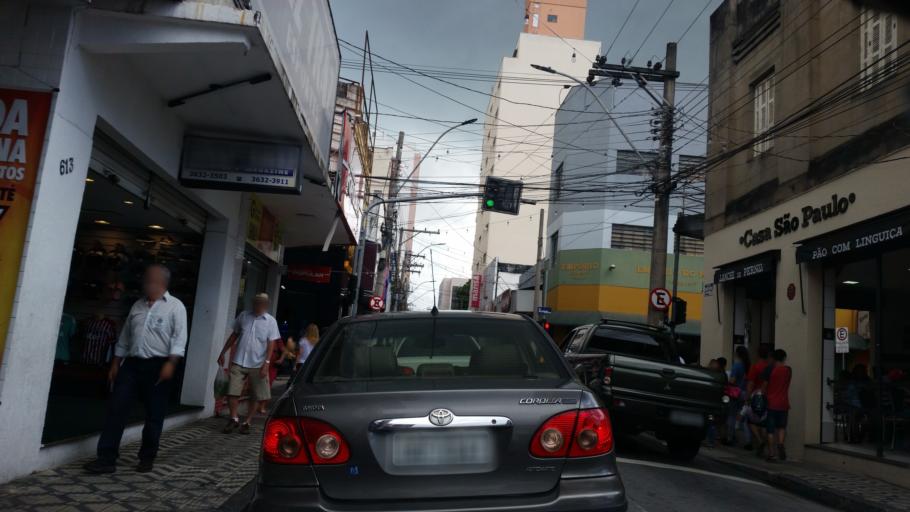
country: BR
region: Sao Paulo
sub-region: Taubate
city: Taubate
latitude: -23.0261
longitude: -45.5544
